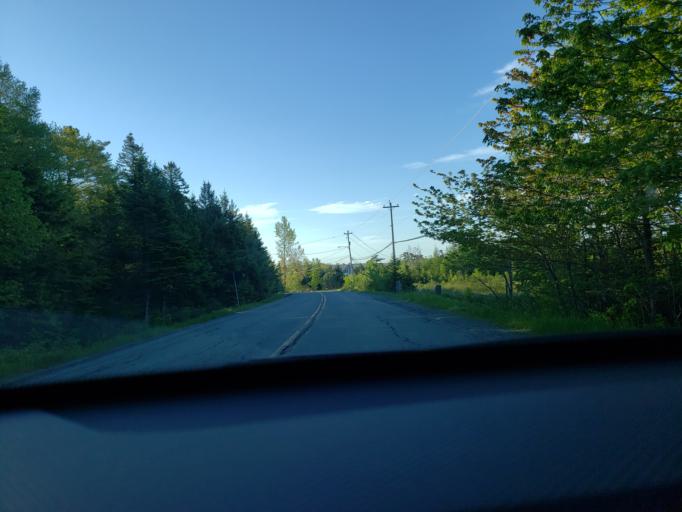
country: CA
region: Nova Scotia
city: Cole Harbour
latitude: 44.7205
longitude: -63.3991
